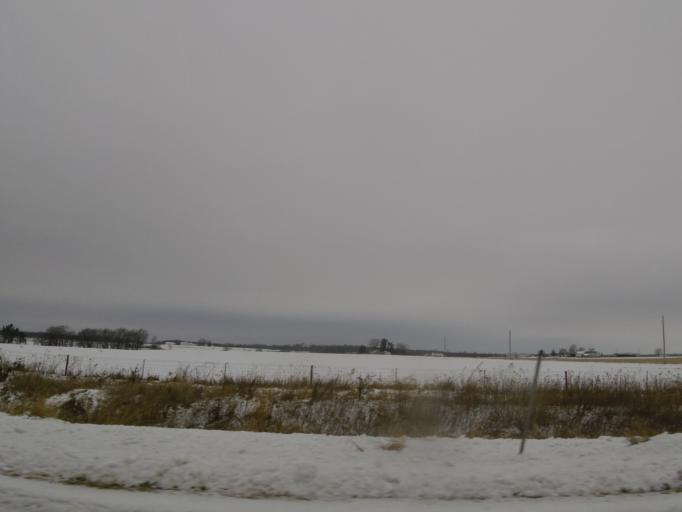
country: US
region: Illinois
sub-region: Hancock County
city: Nauvoo
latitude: 40.6240
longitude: -91.5583
